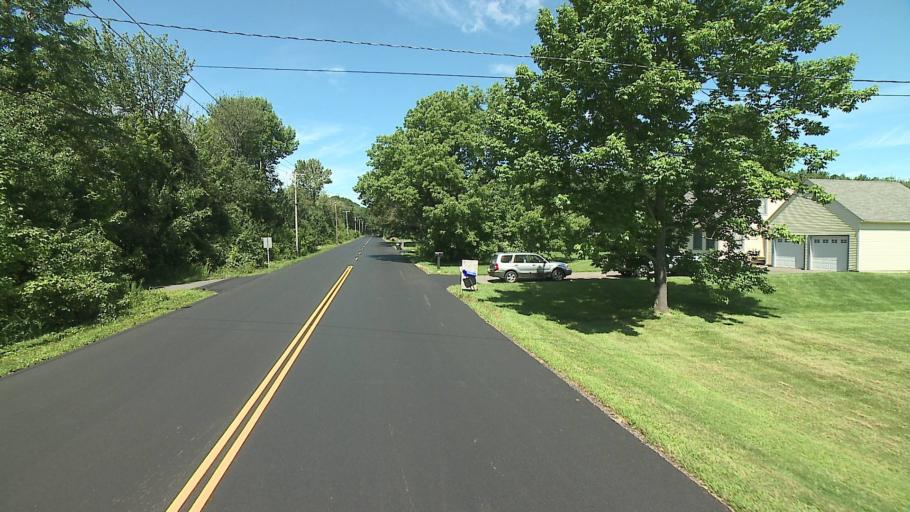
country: US
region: Connecticut
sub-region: Hartford County
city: West Simsbury
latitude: 41.9273
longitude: -72.9123
